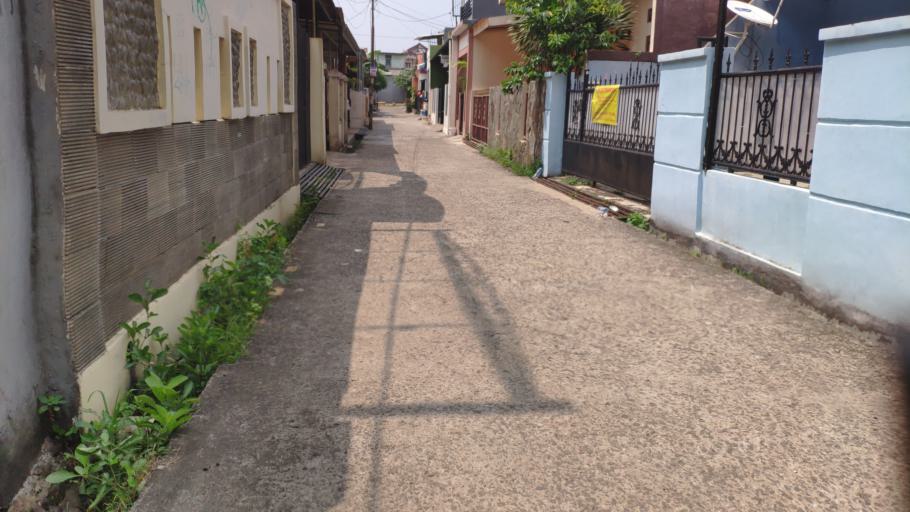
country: ID
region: West Java
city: Pamulang
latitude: -6.3437
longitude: 106.7936
